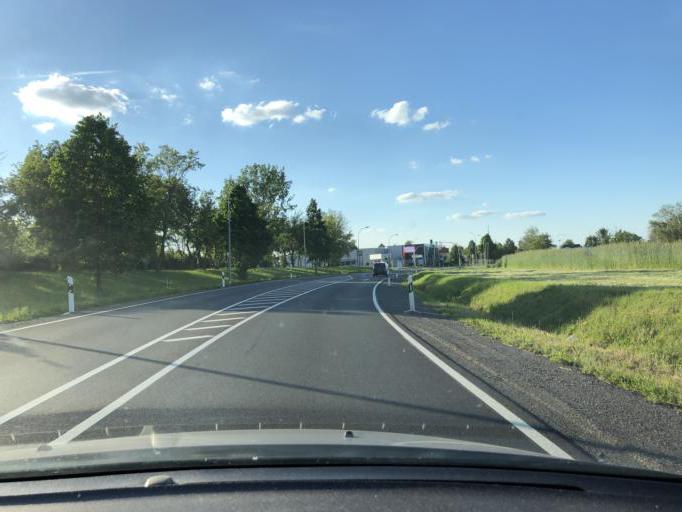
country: DE
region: Saxony
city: Groitzsch
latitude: 51.1457
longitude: 12.2883
